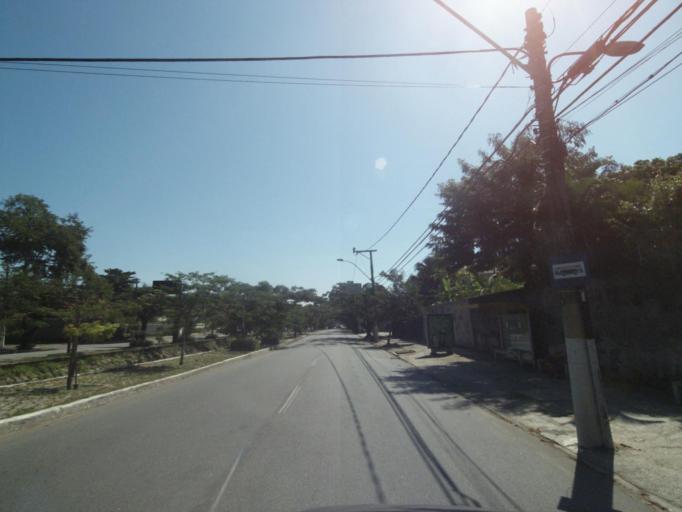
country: BR
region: Rio de Janeiro
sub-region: Niteroi
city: Niteroi
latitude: -22.9141
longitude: -43.0883
